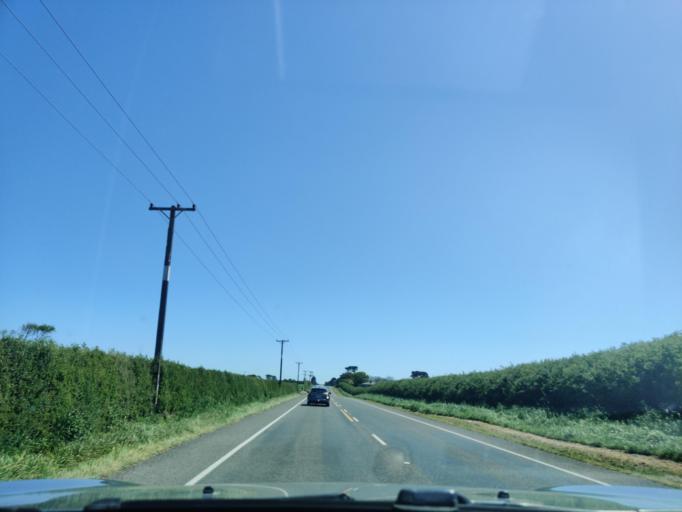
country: NZ
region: Taranaki
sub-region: South Taranaki District
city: Hawera
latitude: -39.6111
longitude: 174.3263
